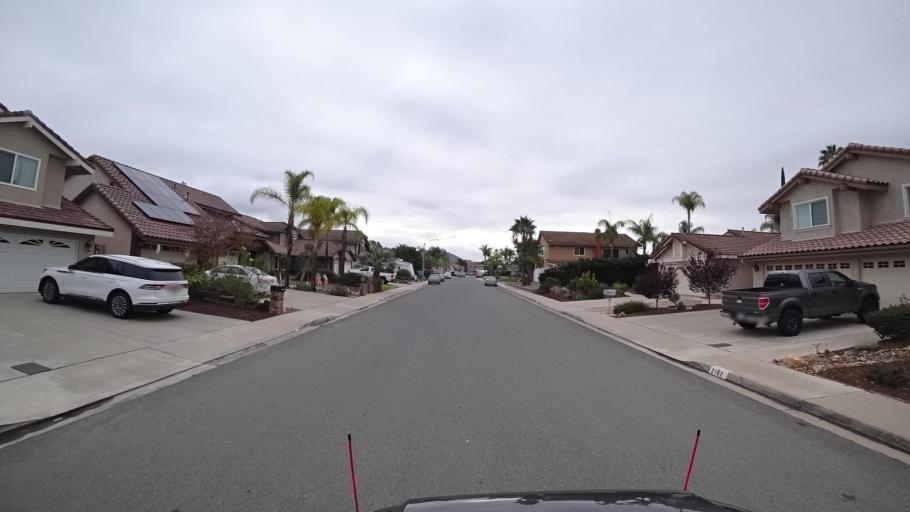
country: US
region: California
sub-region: San Diego County
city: Rancho San Diego
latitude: 32.7594
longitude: -116.9082
